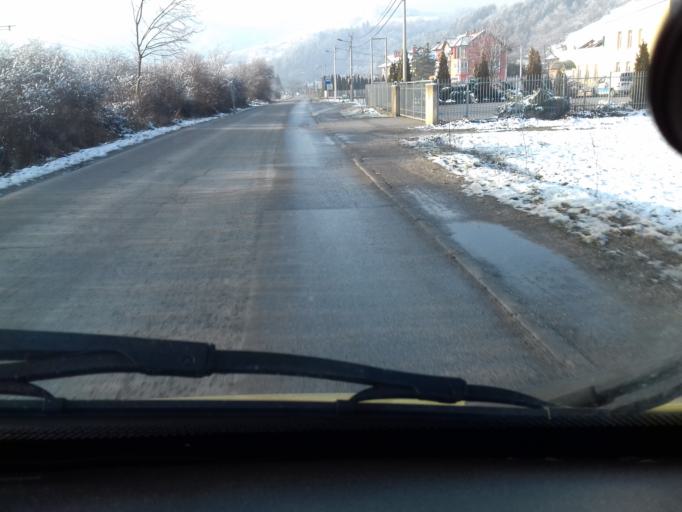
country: BA
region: Federation of Bosnia and Herzegovina
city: Mahala
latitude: 43.9934
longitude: 18.2237
